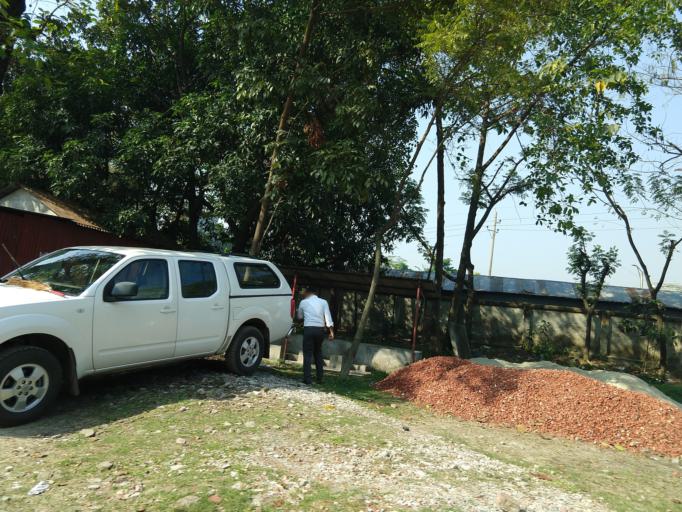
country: BD
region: Dhaka
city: Paltan
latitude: 23.7538
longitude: 90.4044
